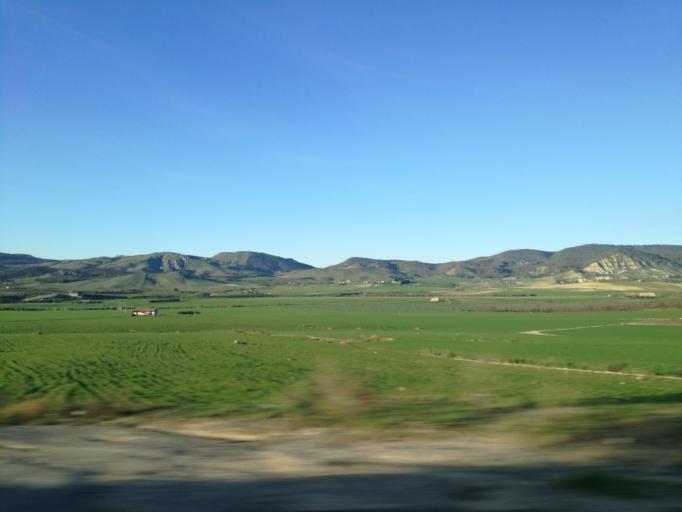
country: IT
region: Sicily
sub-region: Provincia di Caltanissetta
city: Niscemi
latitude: 37.2110
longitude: 14.3960
